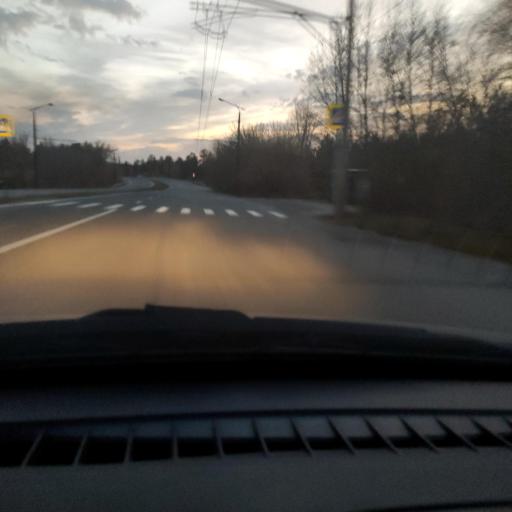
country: RU
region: Samara
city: Zhigulevsk
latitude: 53.5342
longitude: 49.5590
